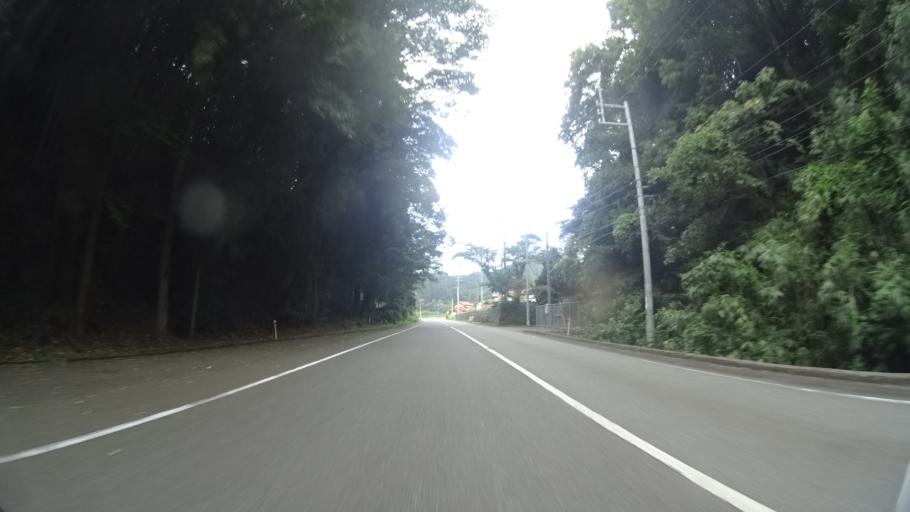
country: JP
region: Yamaguchi
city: Hagi
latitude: 34.5505
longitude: 131.6136
